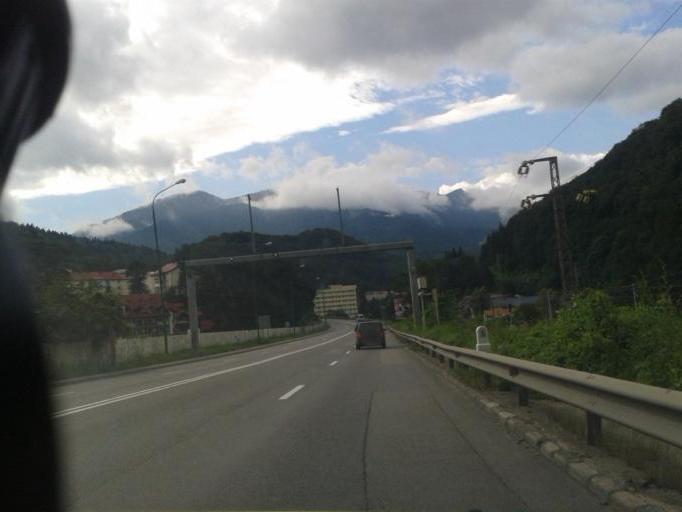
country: RO
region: Prahova
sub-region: Oras Sinaia
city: Sinaia
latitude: 45.3315
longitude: 25.5621
